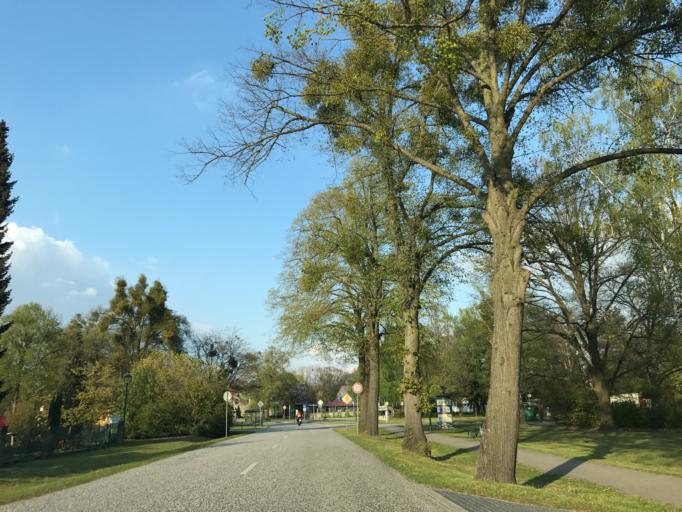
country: DE
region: Brandenburg
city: Wustermark
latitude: 52.5188
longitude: 12.9785
